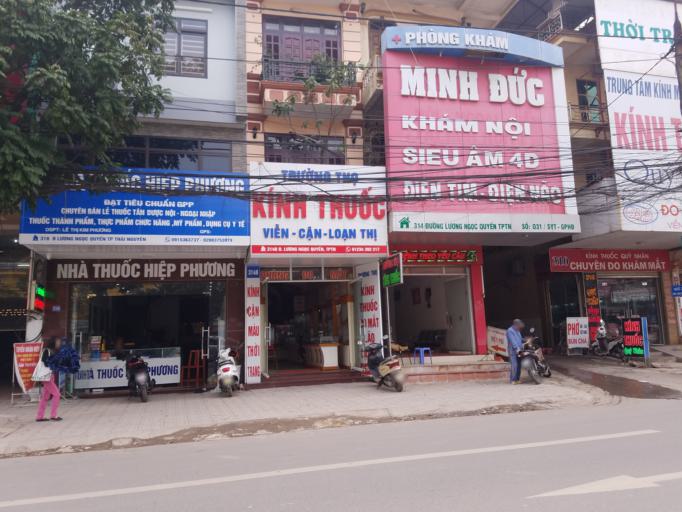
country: VN
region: Thai Nguyen
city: Thanh Pho Thai Nguyen
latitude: 21.5877
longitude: 105.8294
